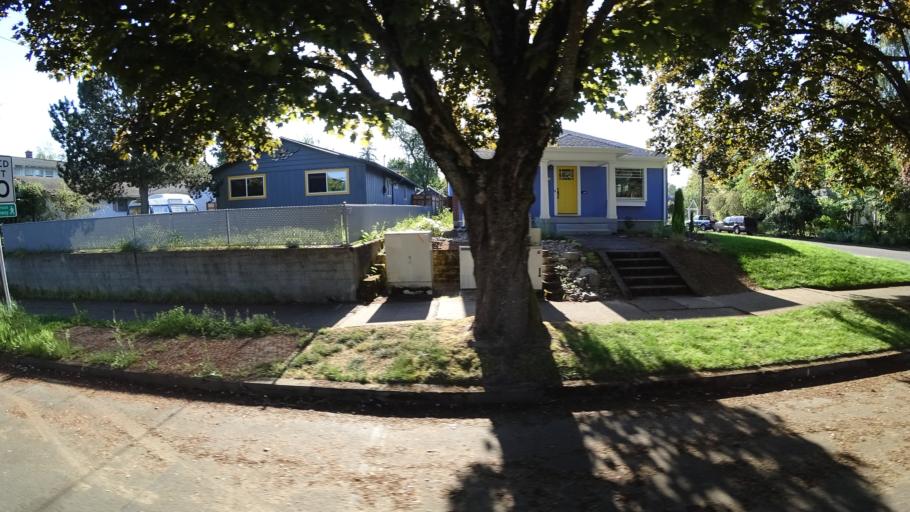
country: US
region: Oregon
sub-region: Multnomah County
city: Portland
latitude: 45.5545
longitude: -122.6852
